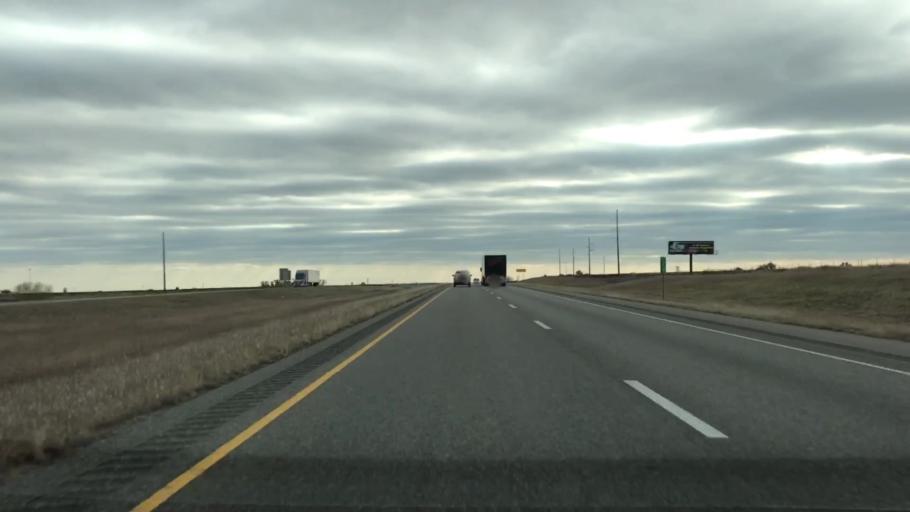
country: US
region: Oklahoma
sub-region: Beckham County
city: Sayre
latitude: 35.3010
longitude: -99.6174
